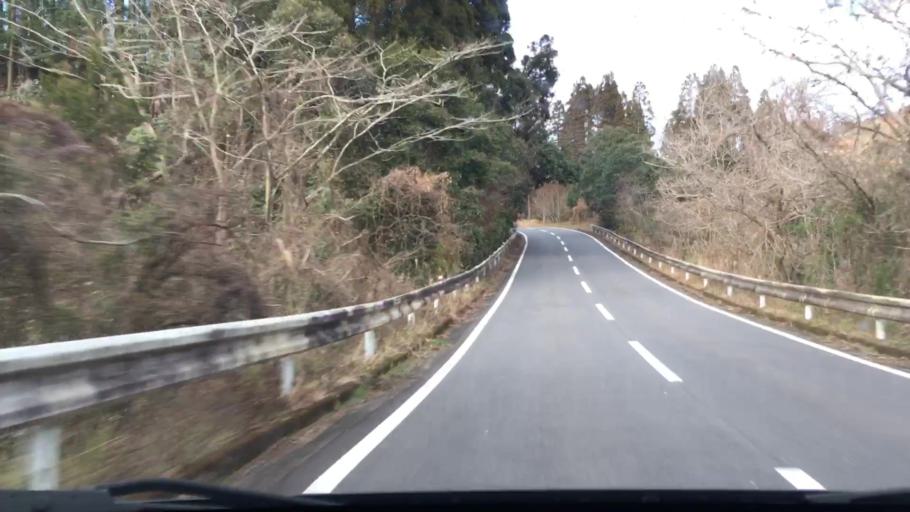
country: JP
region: Miyazaki
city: Nichinan
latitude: 31.7105
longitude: 131.3267
